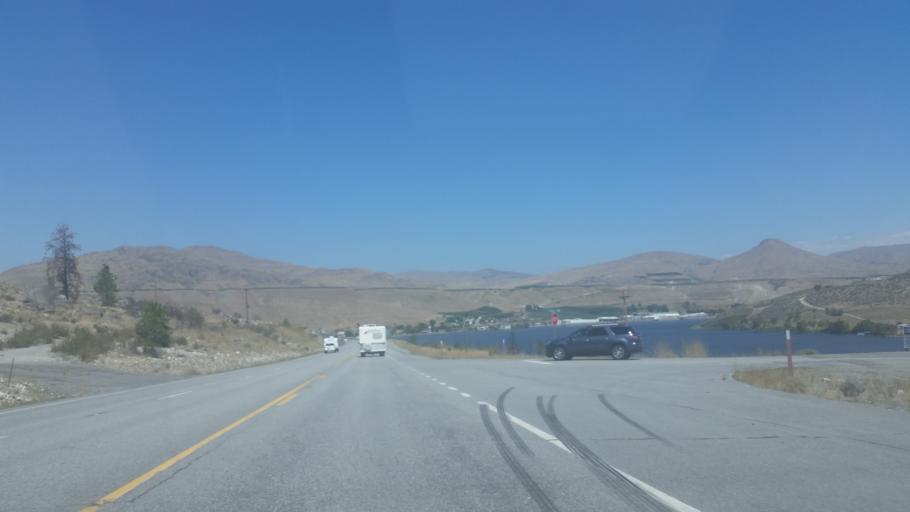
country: US
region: Washington
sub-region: Okanogan County
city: Brewster
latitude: 48.0383
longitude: -119.8956
